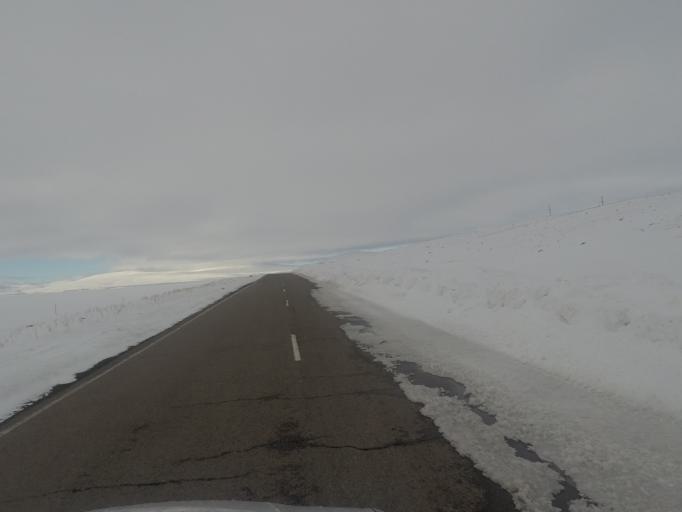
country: GE
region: Samtskhe-Javakheti
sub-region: Ninotsminda
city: Ninotsminda
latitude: 41.4136
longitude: 43.8311
